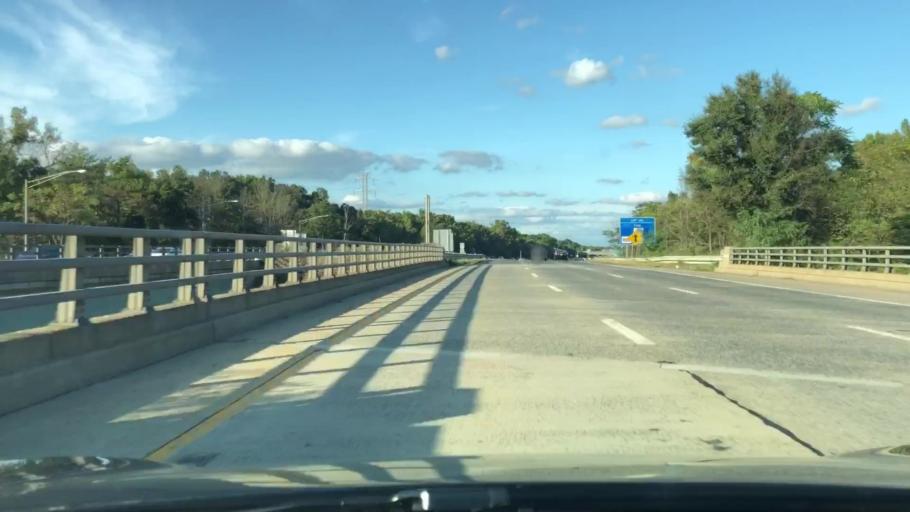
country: US
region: New Jersey
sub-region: Mercer County
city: Mercerville
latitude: 40.2427
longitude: -74.7007
